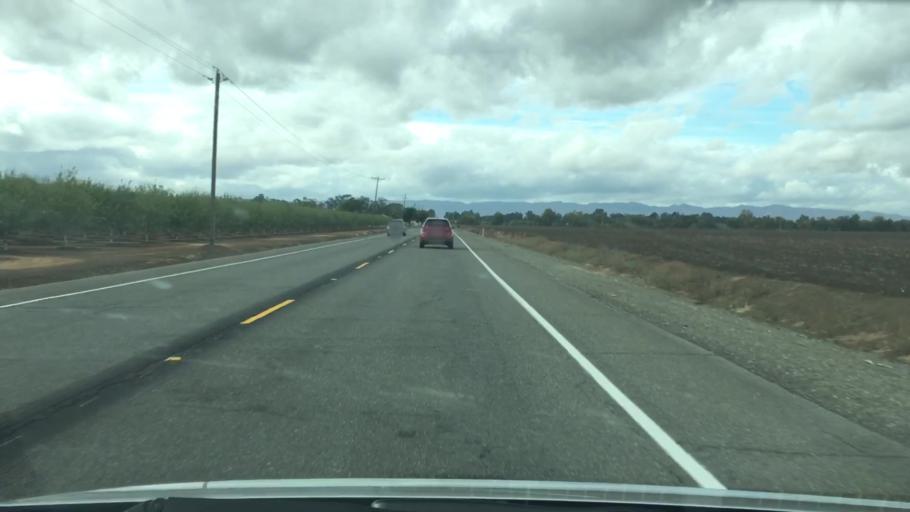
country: US
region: California
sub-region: Yolo County
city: Davis
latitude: 38.5616
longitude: -121.8338
